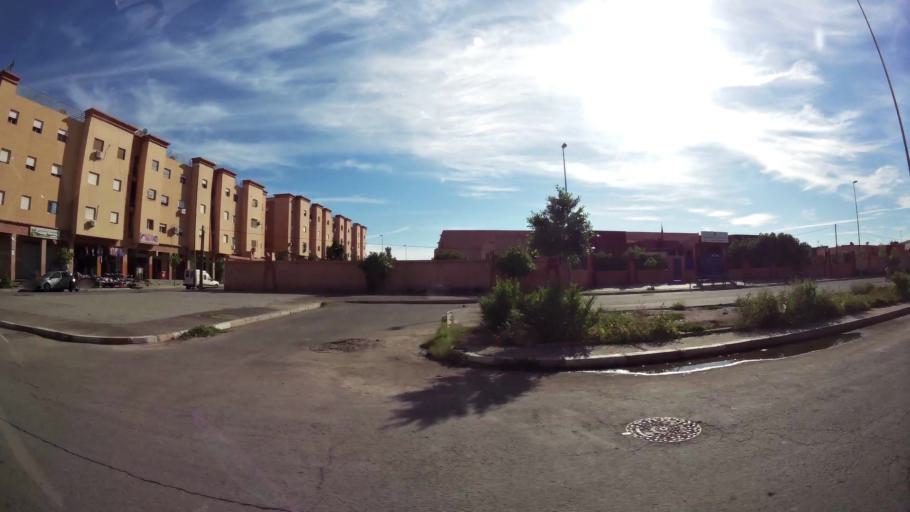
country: MA
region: Marrakech-Tensift-Al Haouz
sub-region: Marrakech
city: Marrakesh
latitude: 31.6875
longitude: -8.0706
